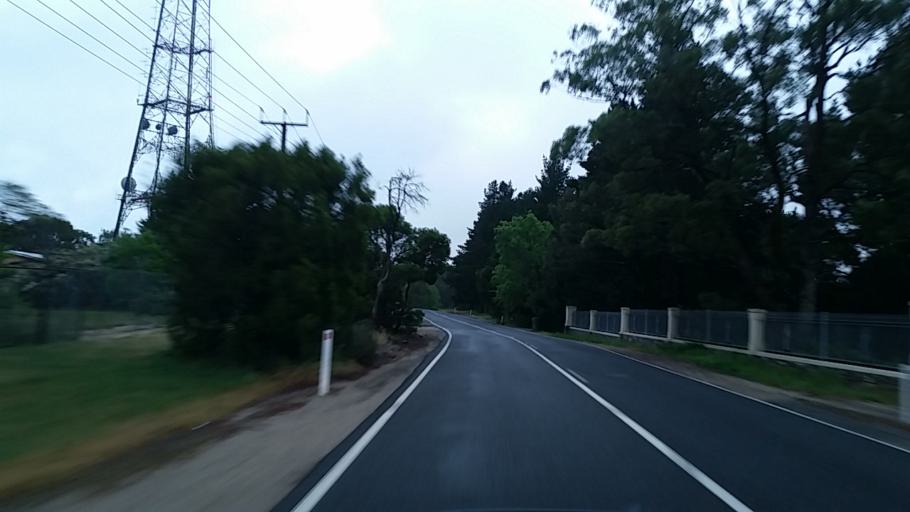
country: AU
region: South Australia
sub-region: Adelaide Hills
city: Crafers
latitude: -34.9803
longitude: 138.7090
